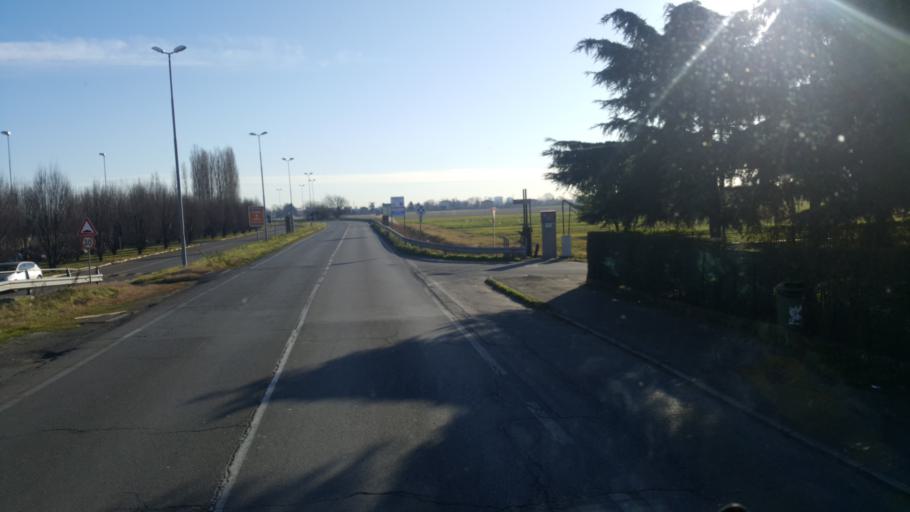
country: IT
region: Emilia-Romagna
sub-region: Provincia di Modena
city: Campogalliano
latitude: 44.6467
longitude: 10.8539
